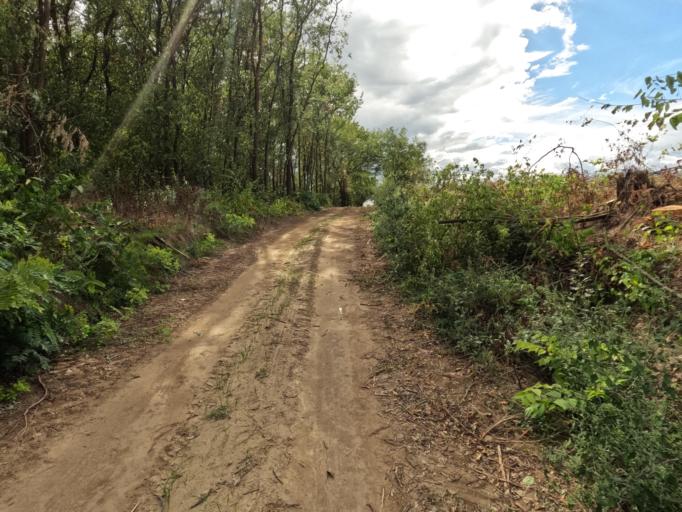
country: HU
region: Tolna
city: Szedres
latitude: 46.5155
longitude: 18.6711
